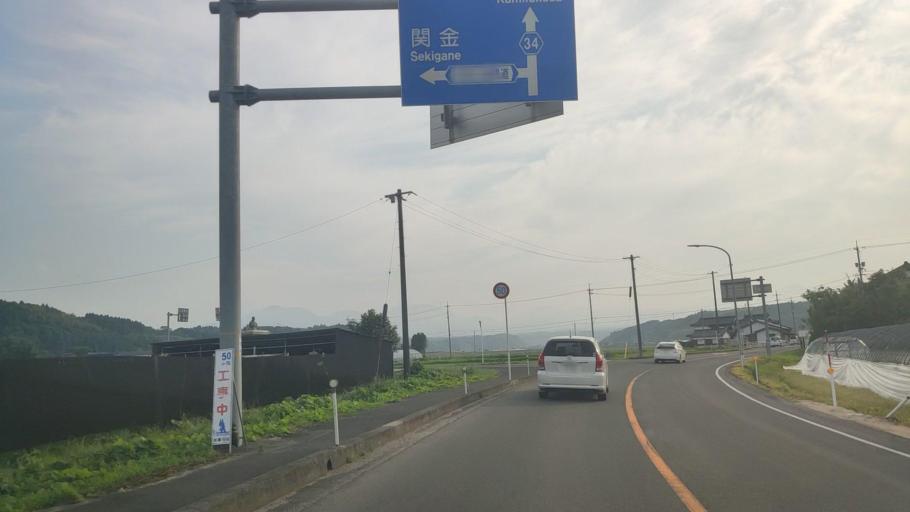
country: JP
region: Tottori
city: Kurayoshi
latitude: 35.4205
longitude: 133.7819
